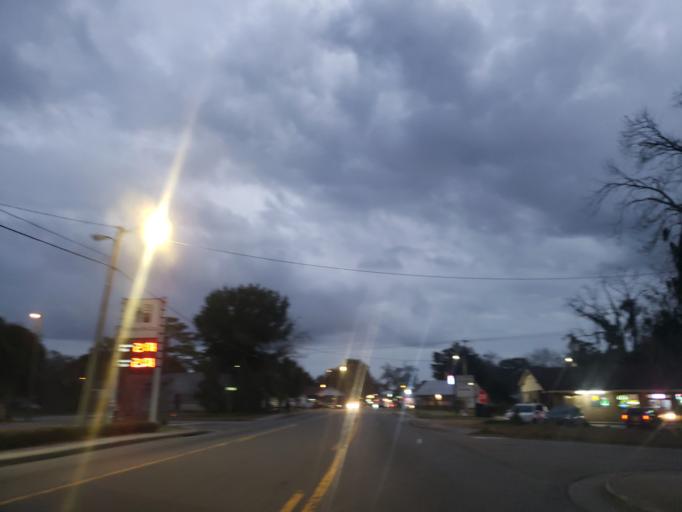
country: US
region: Georgia
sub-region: Chatham County
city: Thunderbolt
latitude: 32.0474
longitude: -81.0645
